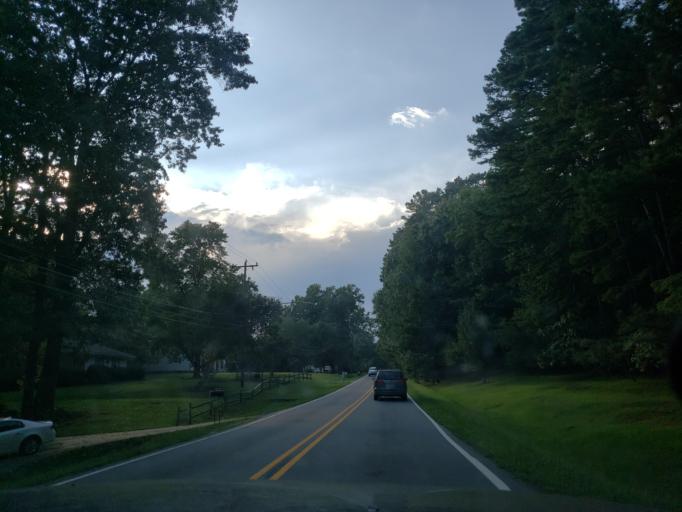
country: US
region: North Carolina
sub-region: Durham County
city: Durham
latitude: 35.9865
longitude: -78.9628
